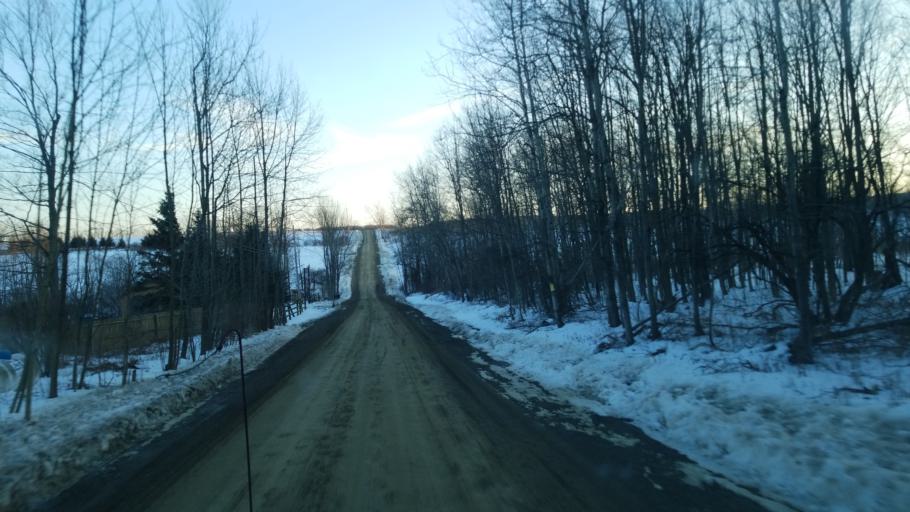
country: US
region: Pennsylvania
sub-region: Tioga County
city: Westfield
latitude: 42.0296
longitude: -77.6196
